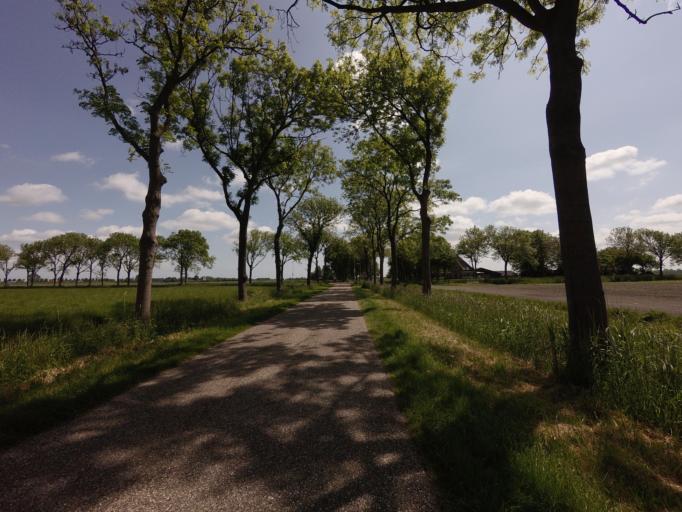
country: NL
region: North Holland
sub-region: Gemeente Beemster
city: Halfweg
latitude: 52.6017
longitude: 4.9146
